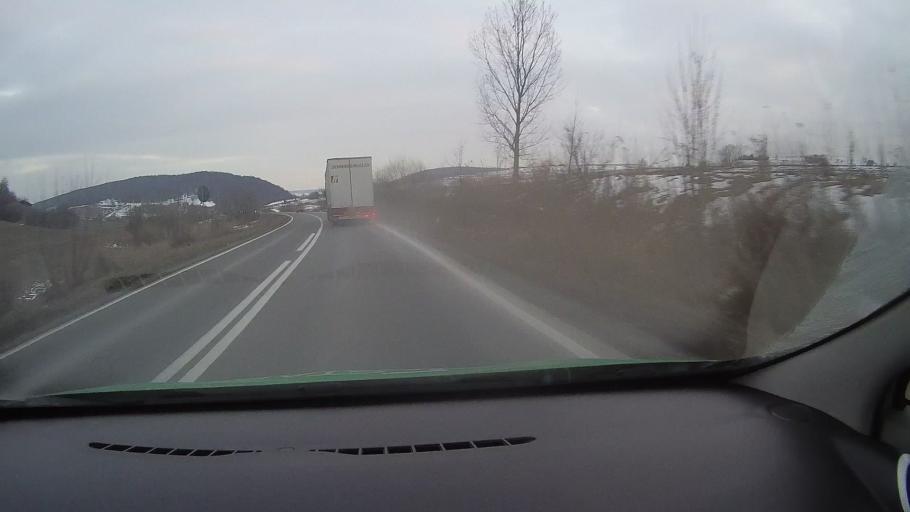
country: RO
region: Harghita
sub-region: Municipiul Odorheiu Secuiesc
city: Odorheiu Secuiesc
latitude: 46.3466
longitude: 25.2643
